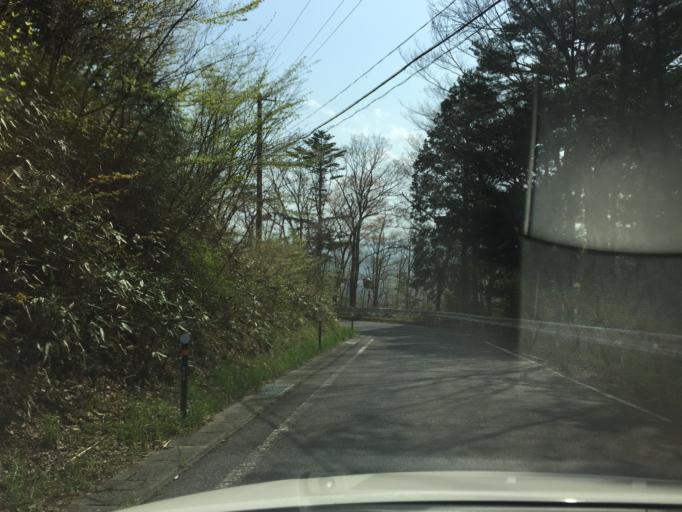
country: JP
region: Fukushima
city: Iwaki
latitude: 37.1995
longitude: 140.8506
